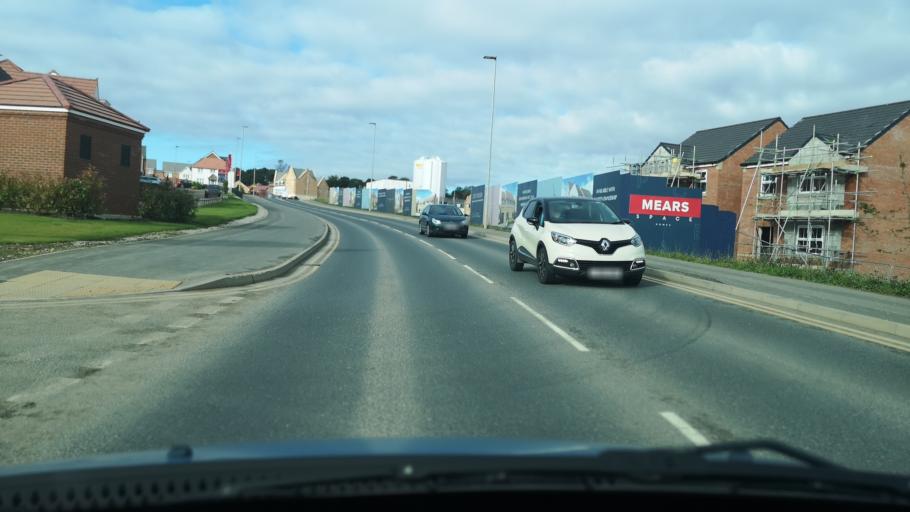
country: GB
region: England
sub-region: City and Borough of Wakefield
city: Wakefield
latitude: 53.6959
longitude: -1.4754
